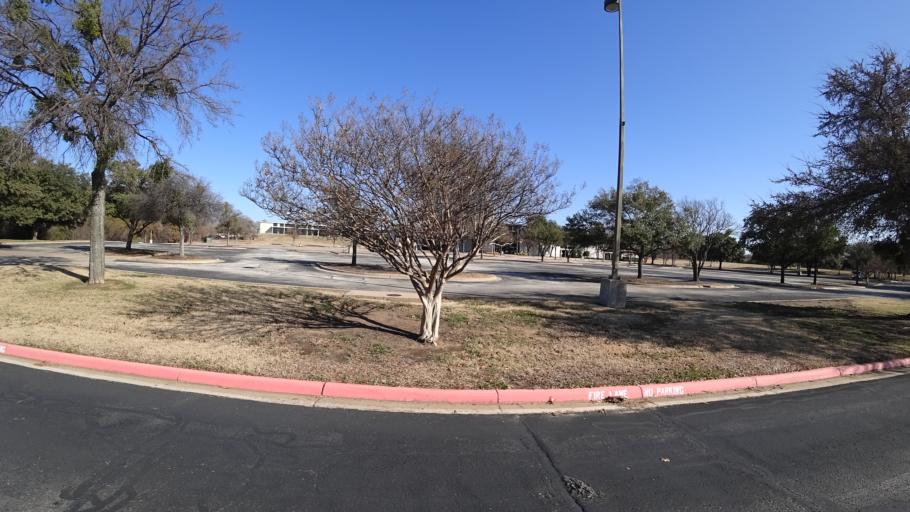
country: US
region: Texas
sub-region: Dallas County
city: Coppell
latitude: 32.9978
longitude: -97.0043
